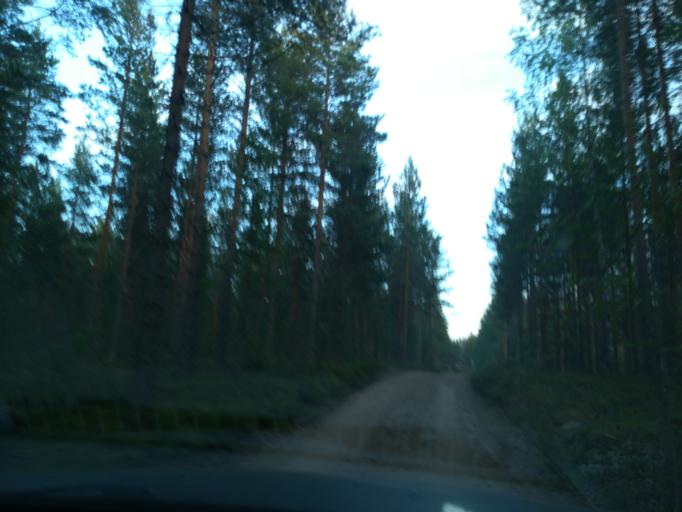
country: FI
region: South Karelia
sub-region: Lappeenranta
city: Joutseno
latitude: 61.3408
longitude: 28.4057
